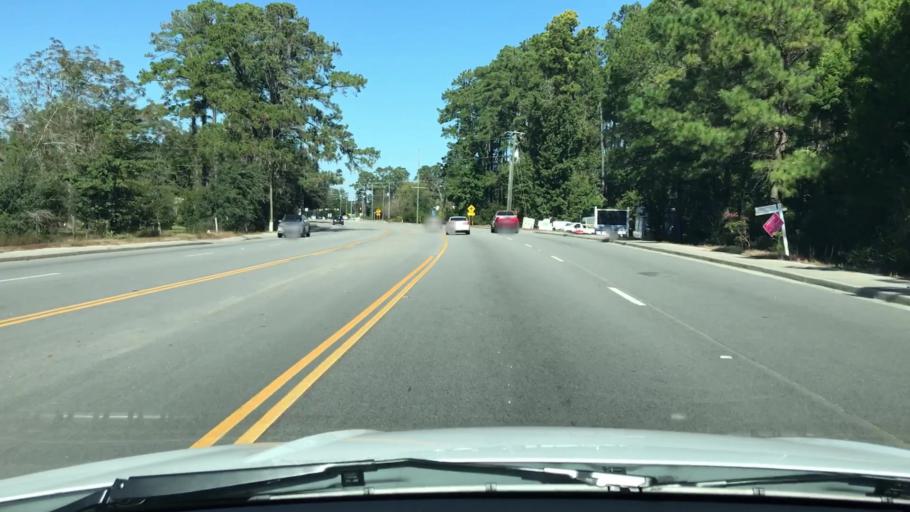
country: US
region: South Carolina
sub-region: Beaufort County
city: Burton
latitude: 32.4377
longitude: -80.7226
